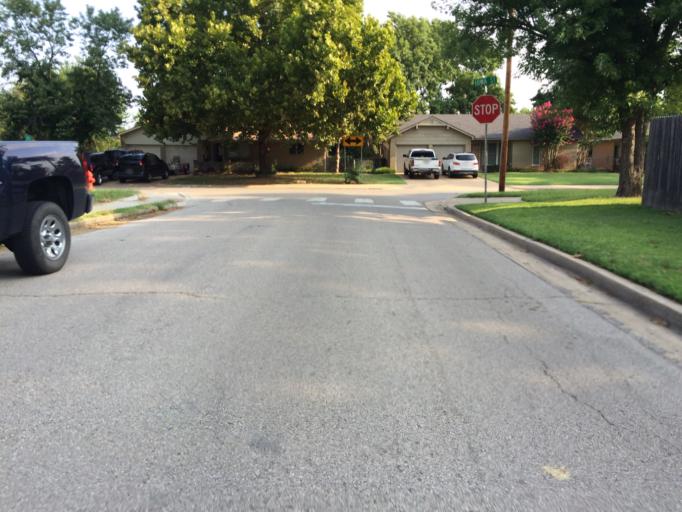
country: US
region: Oklahoma
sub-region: Cleveland County
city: Norman
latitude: 35.2241
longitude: -97.4673
